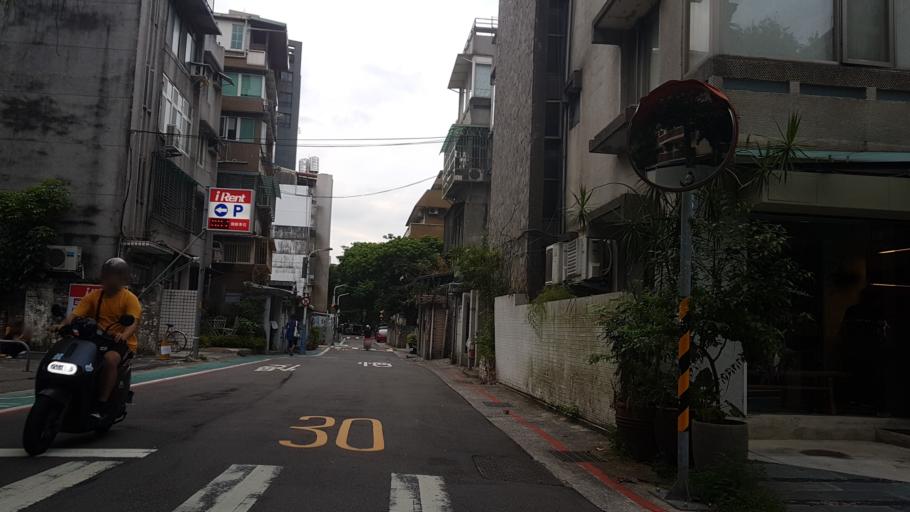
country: TW
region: Taipei
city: Taipei
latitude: 25.0281
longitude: 121.5320
